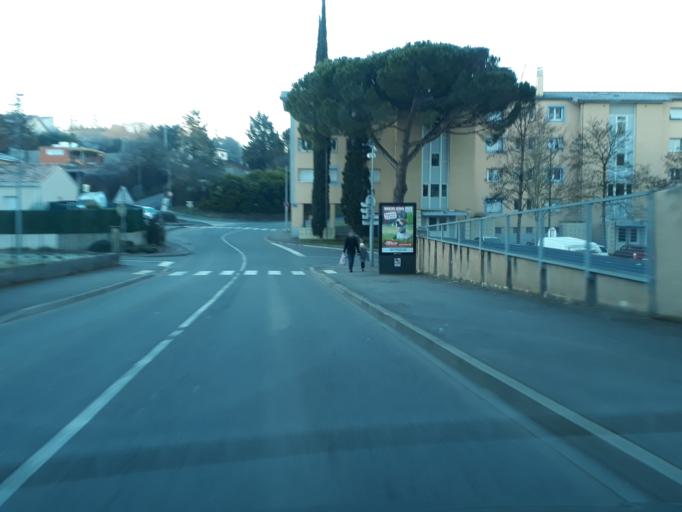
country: FR
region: Midi-Pyrenees
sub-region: Departement du Gers
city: Auch
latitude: 43.6353
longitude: 0.5961
